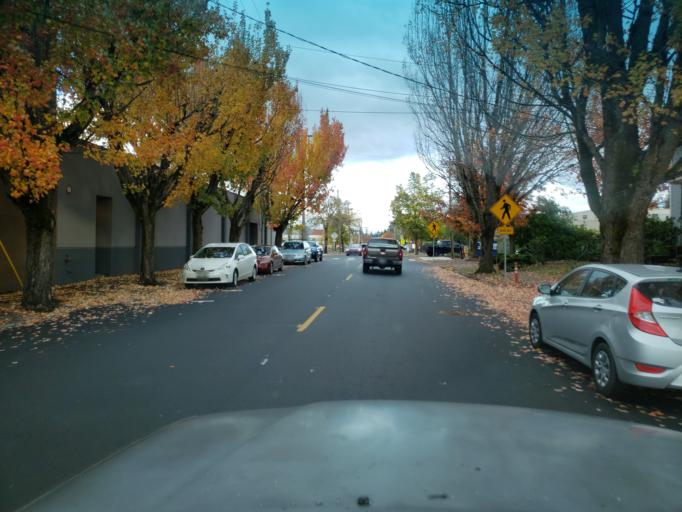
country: US
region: Oregon
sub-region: Yamhill County
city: McMinnville
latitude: 45.2093
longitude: -123.1929
